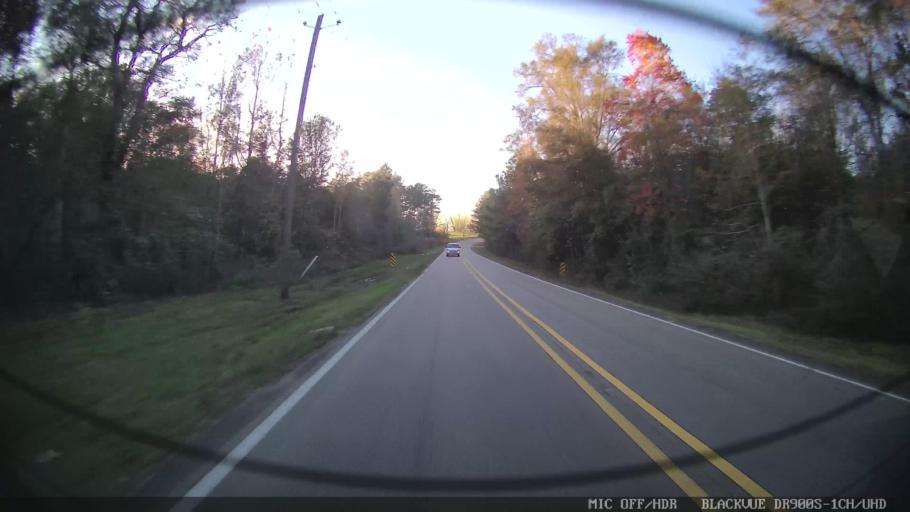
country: US
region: Mississippi
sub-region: Lamar County
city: Lumberton
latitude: 30.9942
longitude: -89.3814
